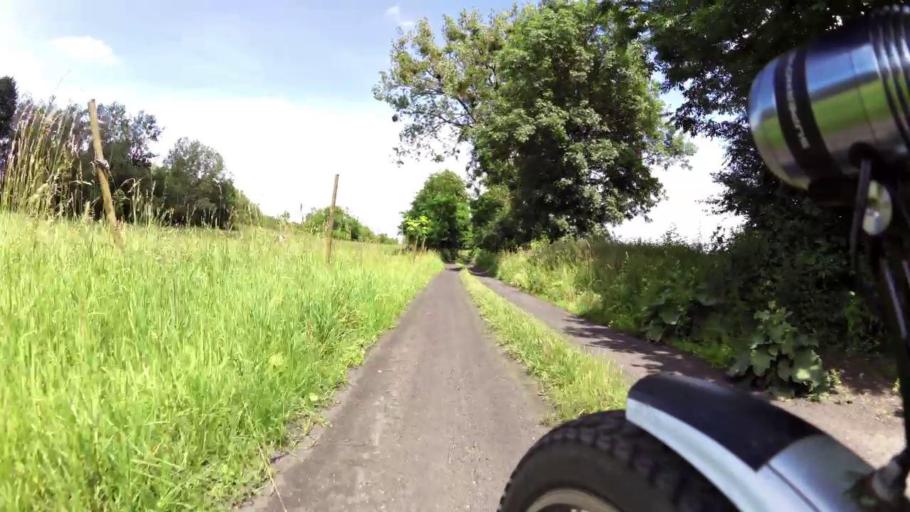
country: PL
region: West Pomeranian Voivodeship
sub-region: Powiat choszczenski
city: Choszczno
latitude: 53.1955
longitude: 15.4386
